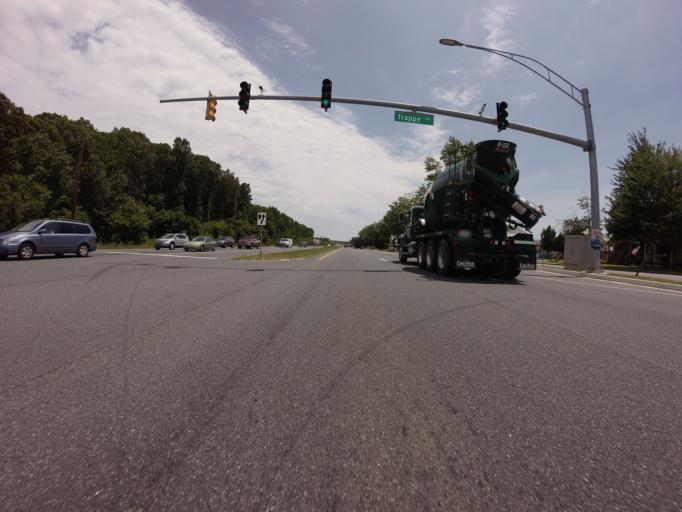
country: US
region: Maryland
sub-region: Baltimore County
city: Essex
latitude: 39.2804
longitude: -76.4850
